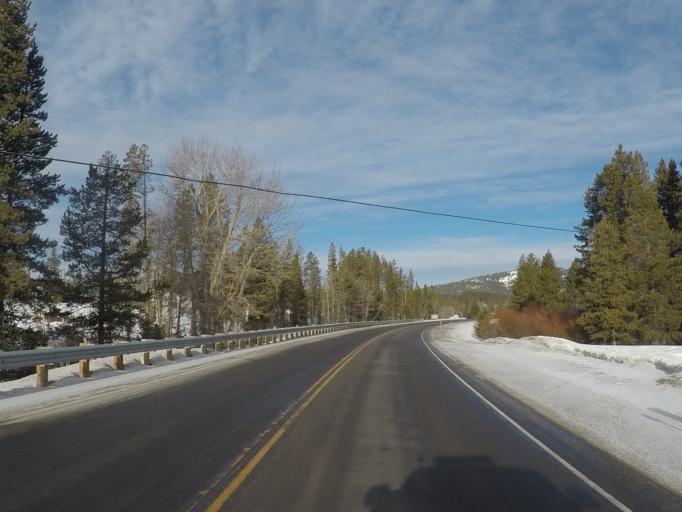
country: US
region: Montana
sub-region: Deer Lodge County
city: Anaconda
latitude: 46.1601
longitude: -113.1386
